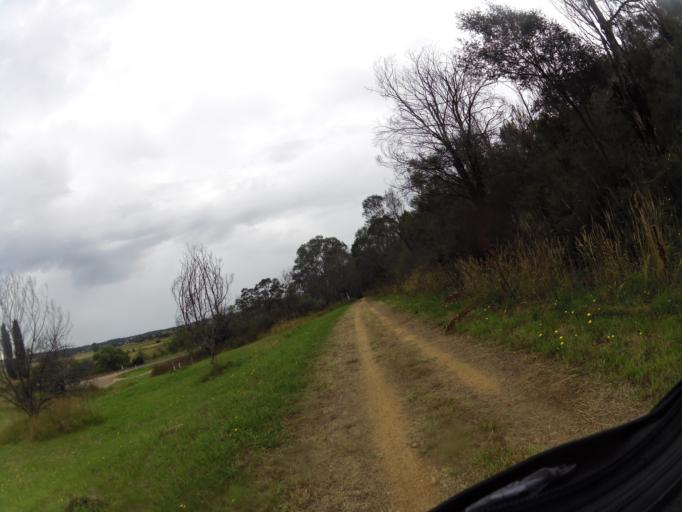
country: AU
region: Victoria
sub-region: East Gippsland
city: Bairnsdale
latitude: -37.7097
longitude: 147.8138
